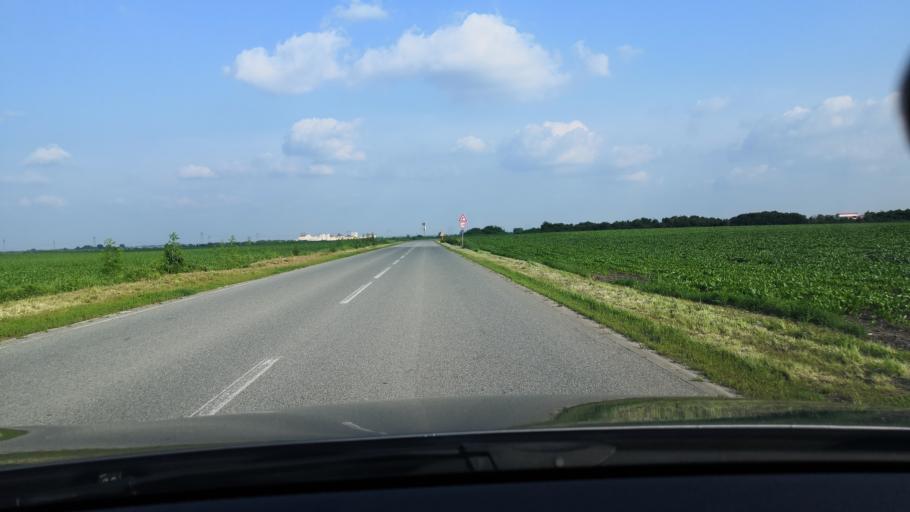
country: RS
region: Autonomna Pokrajina Vojvodina
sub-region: Sremski Okrug
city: Ingija
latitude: 45.0781
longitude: 20.1214
